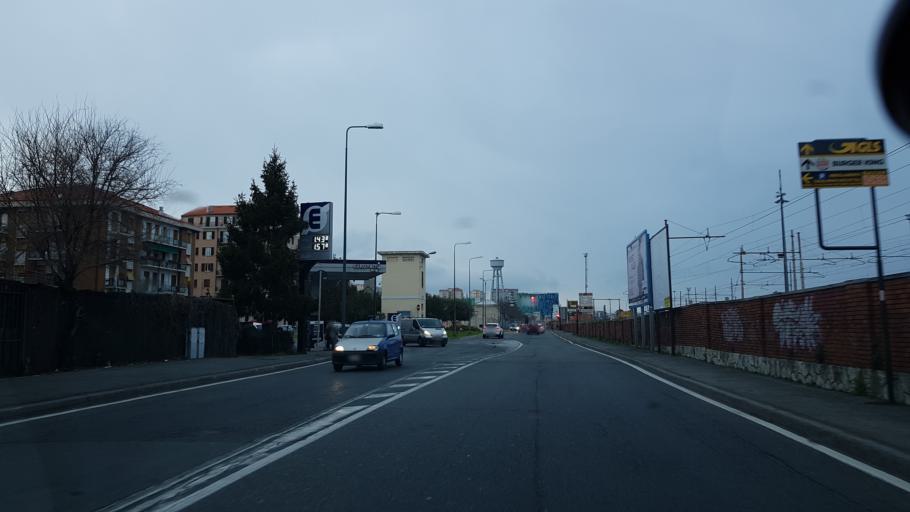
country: IT
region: Liguria
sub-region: Provincia di Savona
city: Savona
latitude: 44.2955
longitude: 8.4558
